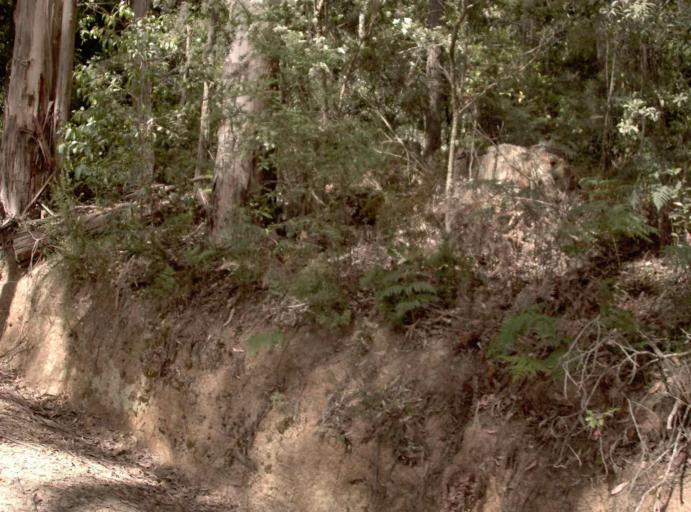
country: AU
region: Victoria
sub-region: East Gippsland
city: Lakes Entrance
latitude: -37.5838
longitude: 148.7264
